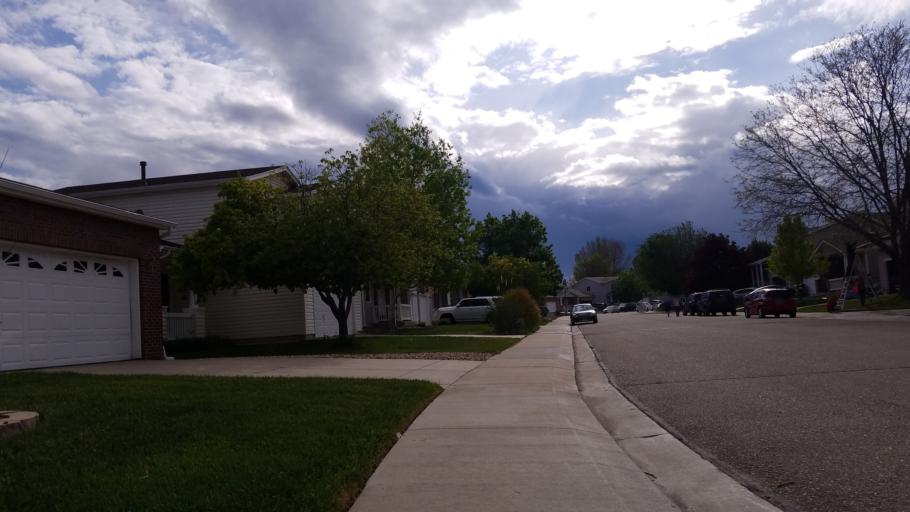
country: US
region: Colorado
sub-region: Boulder County
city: Longmont
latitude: 40.1789
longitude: -105.0713
